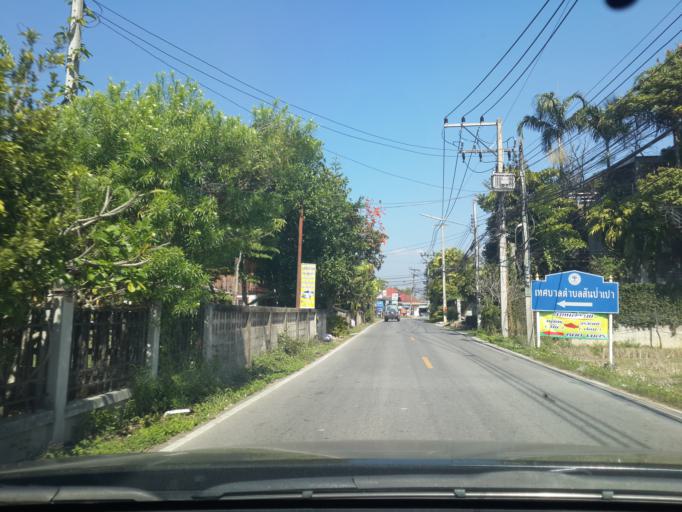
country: TH
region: Chiang Mai
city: San Sai
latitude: 18.8572
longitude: 99.0882
